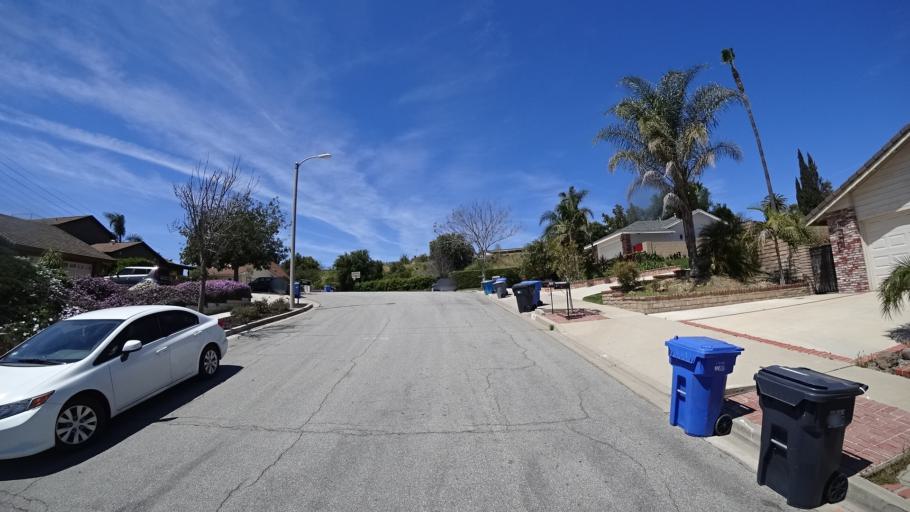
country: US
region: California
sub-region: Ventura County
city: Moorpark
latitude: 34.2312
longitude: -118.8594
